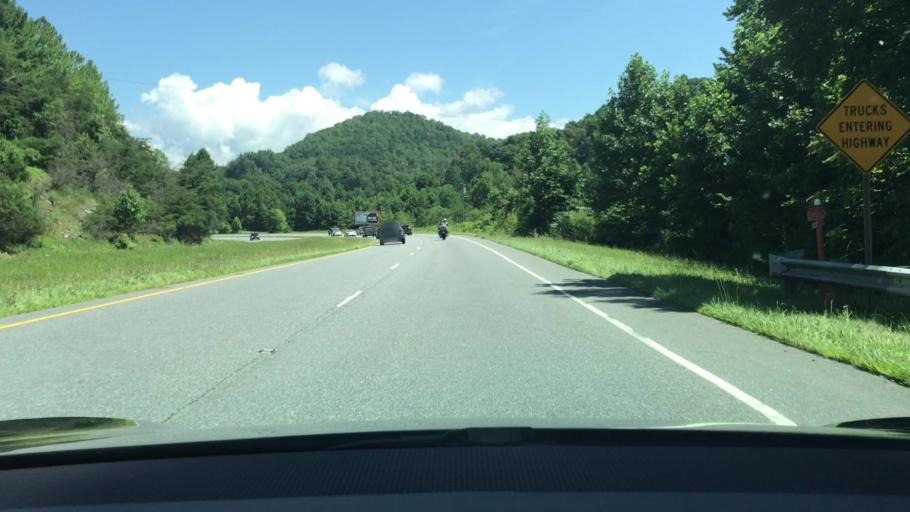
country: US
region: North Carolina
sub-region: Jackson County
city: Sylva
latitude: 35.3041
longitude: -83.2597
